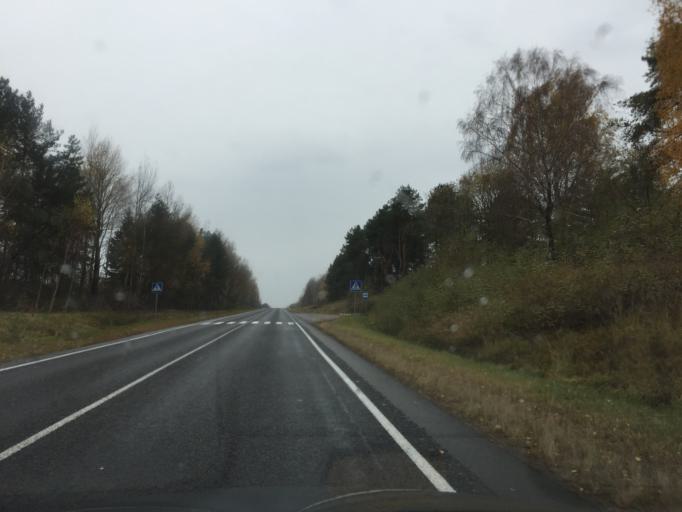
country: BY
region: Gomel
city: Karma
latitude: 53.3102
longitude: 30.7417
